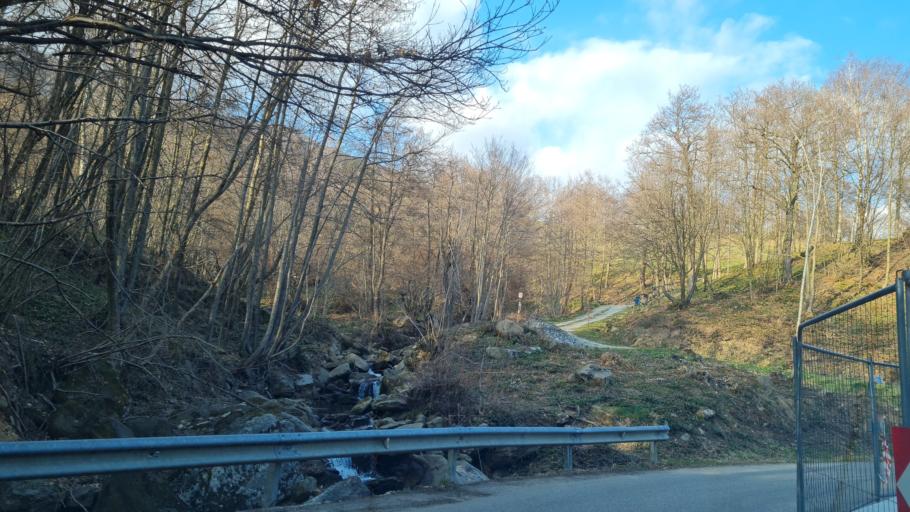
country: IT
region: Piedmont
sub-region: Provincia di Biella
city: Donato
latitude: 45.5482
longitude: 7.9178
